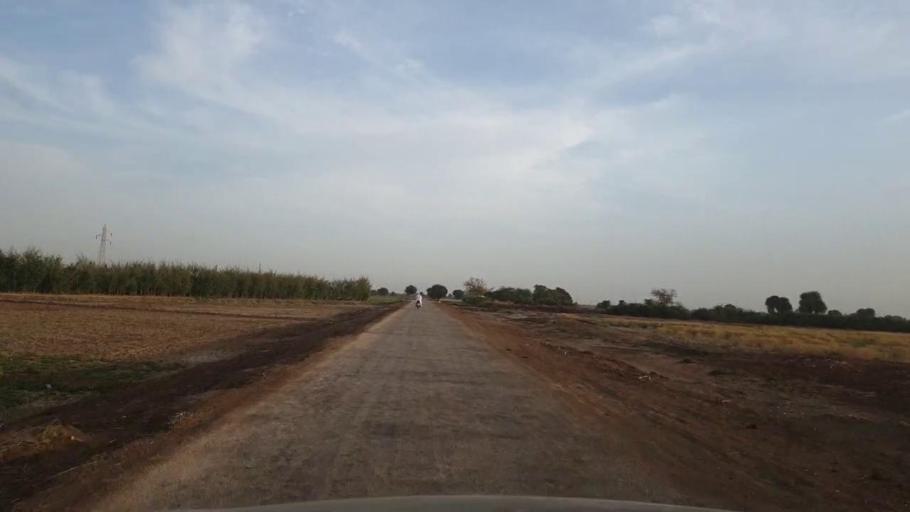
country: PK
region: Sindh
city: Kunri
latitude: 25.1674
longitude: 69.5458
